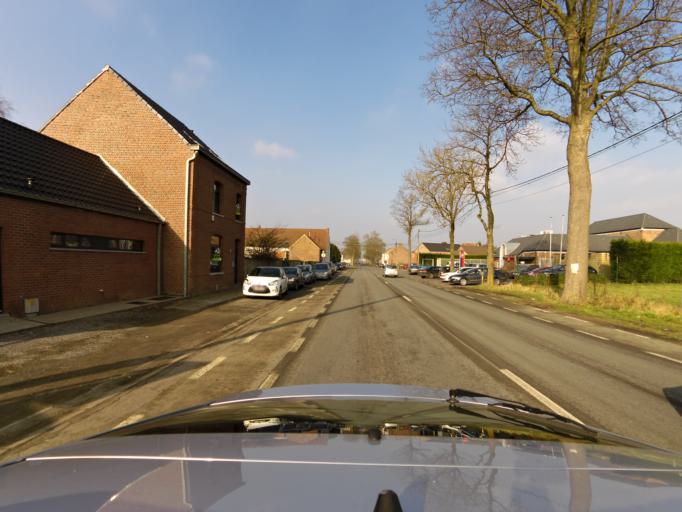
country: BE
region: Wallonia
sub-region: Province du Hainaut
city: Bernissart
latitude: 50.5171
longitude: 3.6682
